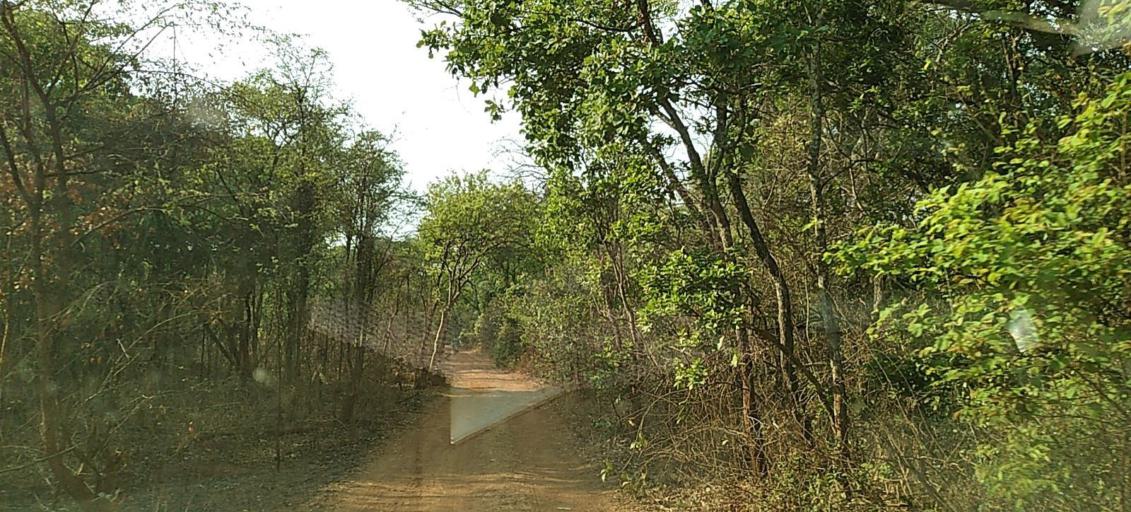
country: ZM
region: Copperbelt
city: Kalulushi
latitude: -12.9646
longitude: 27.7123
